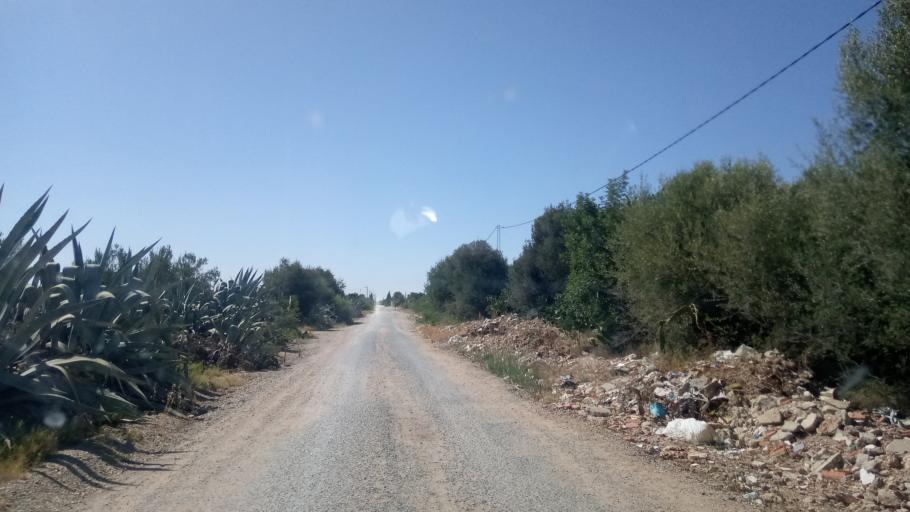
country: TN
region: Al Qayrawan
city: Sbikha
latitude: 36.1276
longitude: 10.0850
